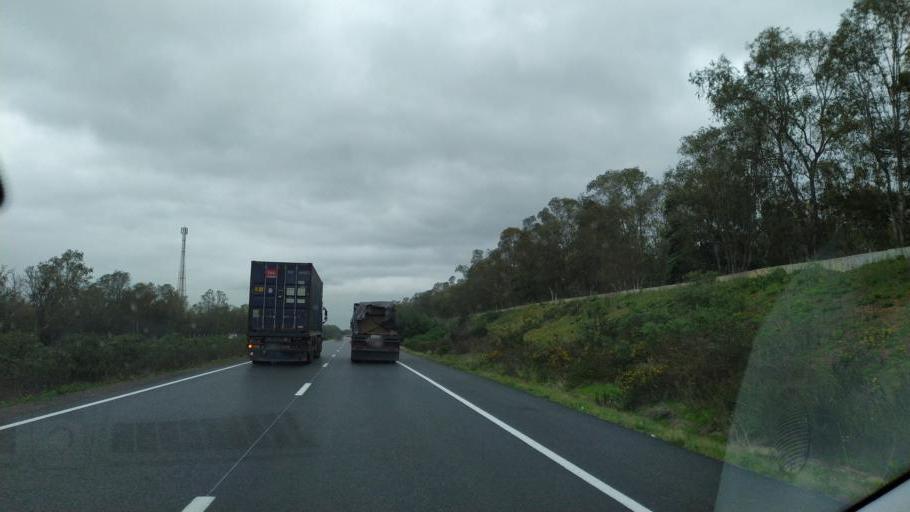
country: MA
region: Gharb-Chrarda-Beni Hssen
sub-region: Kenitra Province
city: Kenitra
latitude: 34.2148
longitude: -6.6096
